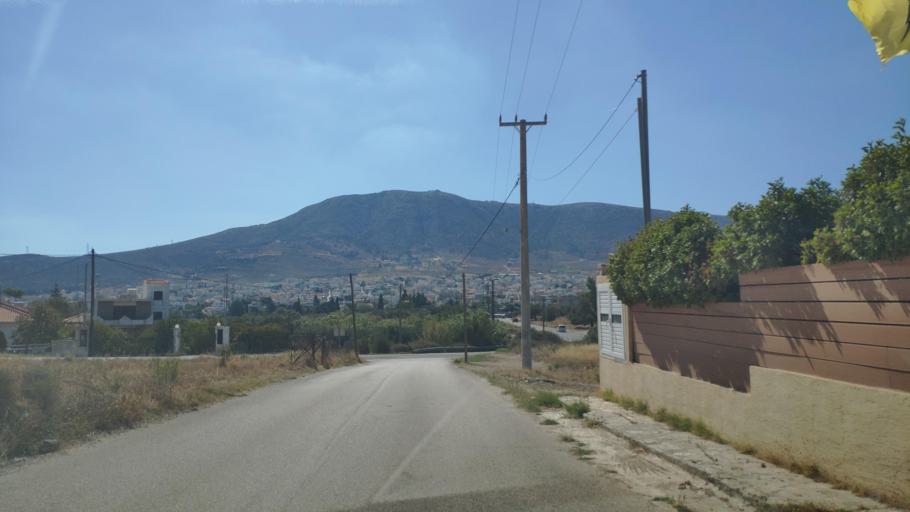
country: GR
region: Attica
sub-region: Nomarchia Anatolikis Attikis
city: Keratea
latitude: 37.8140
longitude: 23.9866
